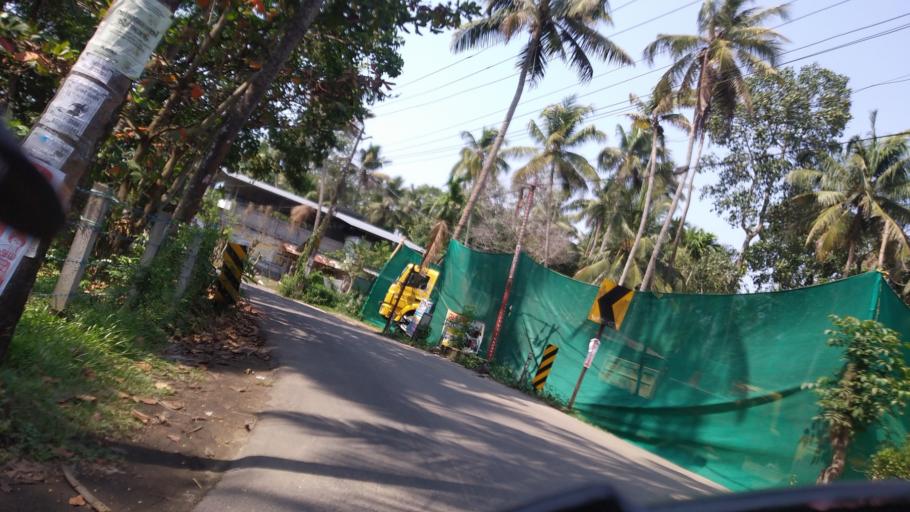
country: IN
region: Kerala
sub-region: Thrissur District
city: Kodungallur
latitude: 10.2465
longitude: 76.1495
